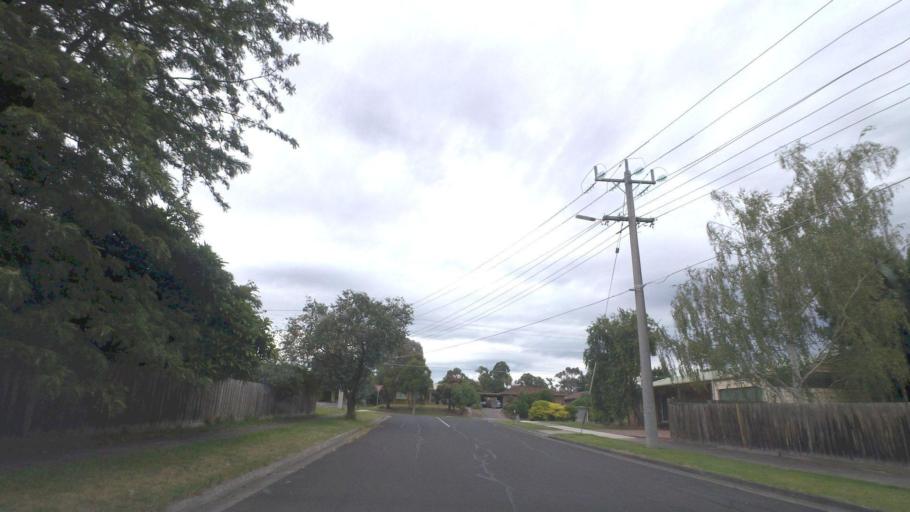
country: AU
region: Victoria
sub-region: Yarra Ranges
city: Lilydale
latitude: -37.7481
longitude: 145.3637
